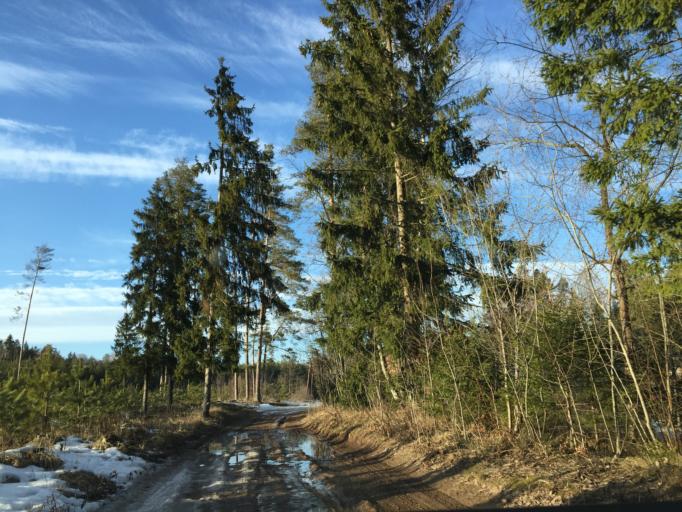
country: LV
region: Lecava
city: Iecava
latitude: 56.6906
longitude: 24.0771
